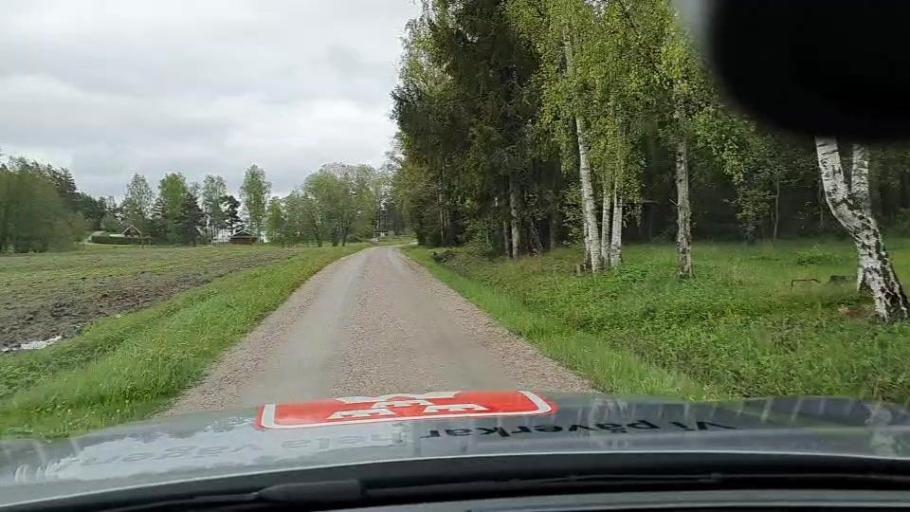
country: SE
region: Soedermanland
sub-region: Nykopings Kommun
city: Svalsta
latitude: 58.6205
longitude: 16.9382
